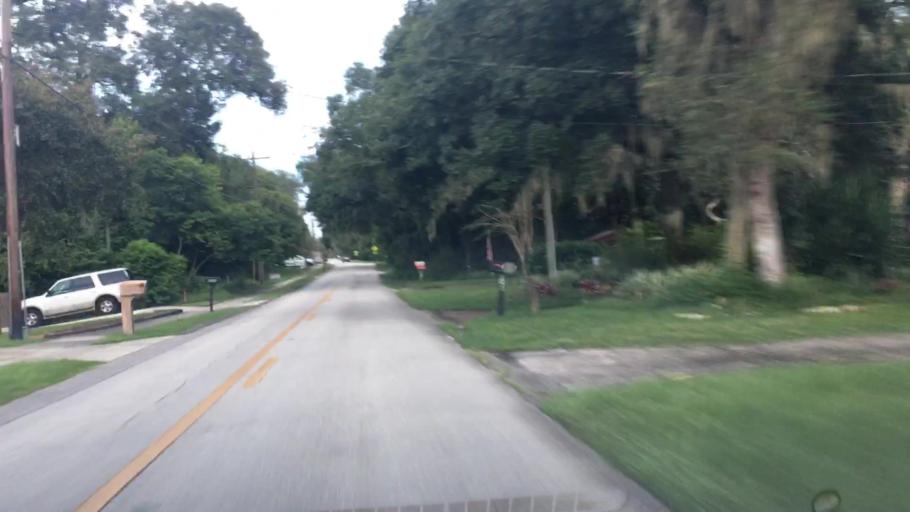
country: US
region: Florida
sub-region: Volusia County
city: DeBary
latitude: 28.8783
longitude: -81.3021
